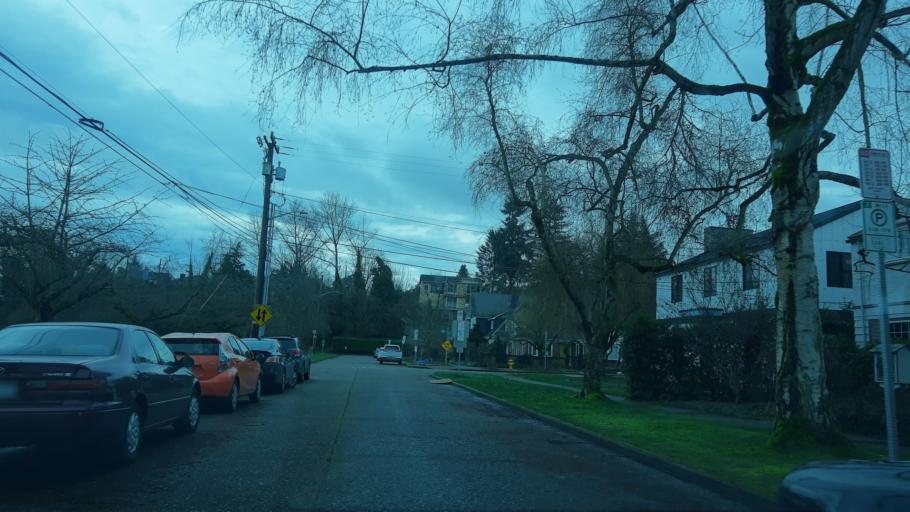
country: US
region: Washington
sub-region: King County
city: Seattle
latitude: 47.6410
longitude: -122.3097
